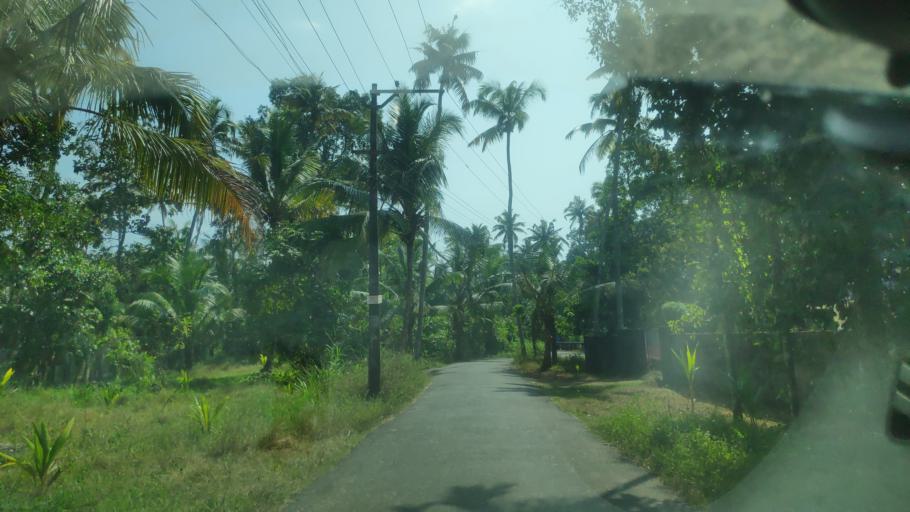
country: IN
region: Kerala
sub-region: Alappuzha
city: Vayalar
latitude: 9.6615
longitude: 76.3048
